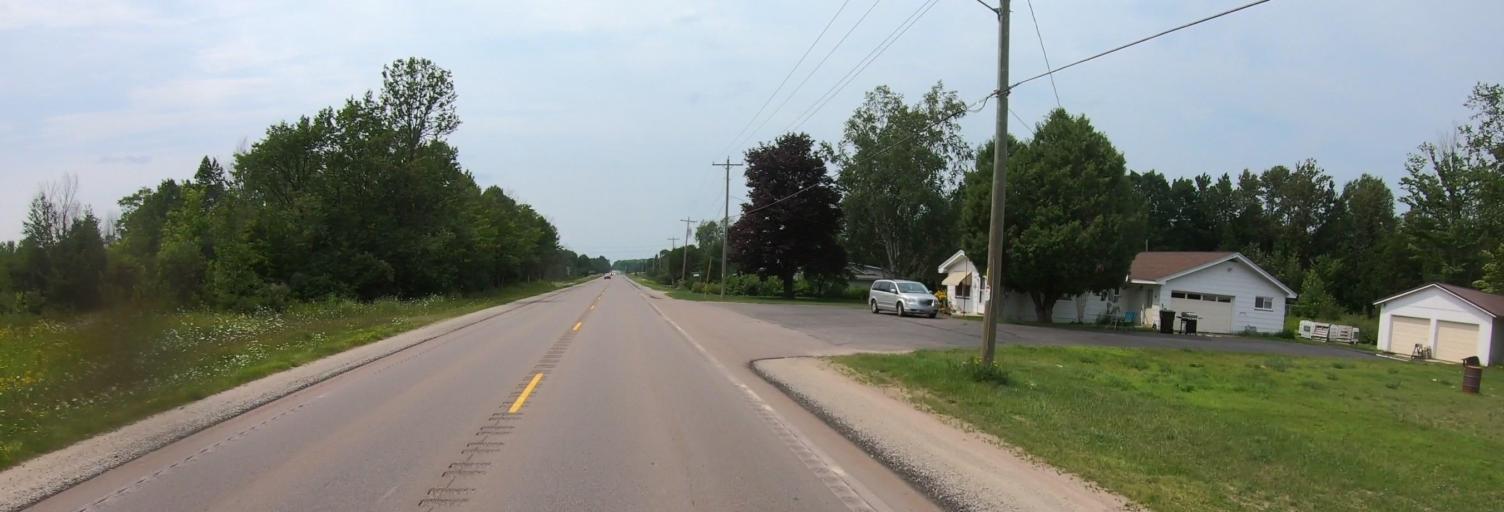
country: US
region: Michigan
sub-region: Alger County
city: Munising
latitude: 46.3549
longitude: -86.9733
